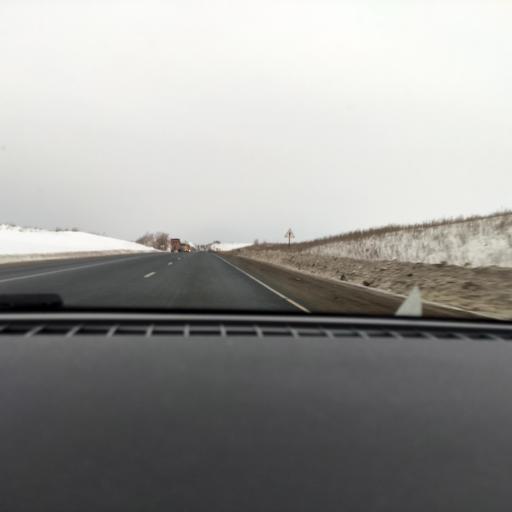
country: RU
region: Samara
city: Novosemeykino
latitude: 53.4024
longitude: 50.3950
